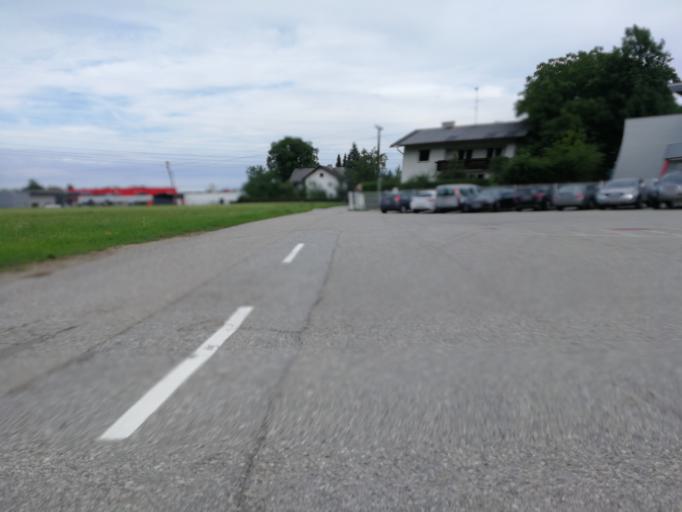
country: AT
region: Salzburg
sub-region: Politischer Bezirk Salzburg-Umgebung
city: Bergheim
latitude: 47.8416
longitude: 13.0327
